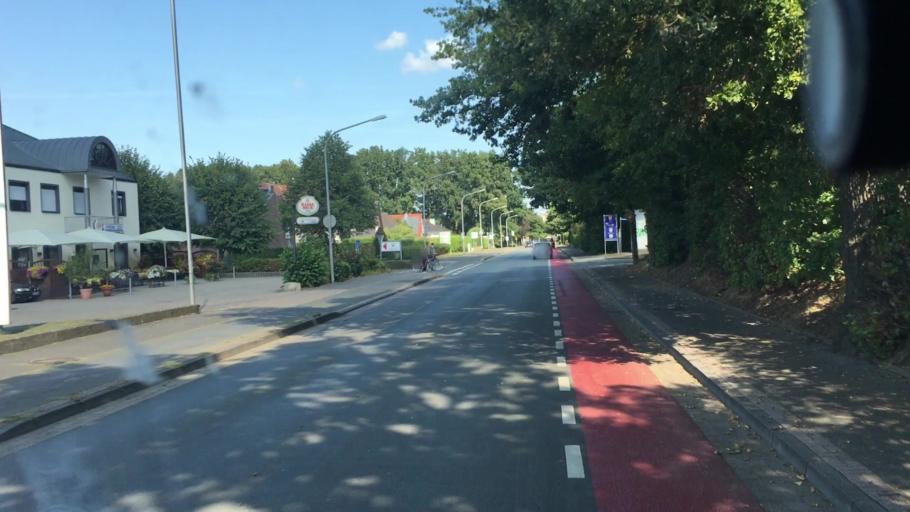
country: DE
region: Lower Saxony
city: Lohne
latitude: 52.6546
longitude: 8.2421
